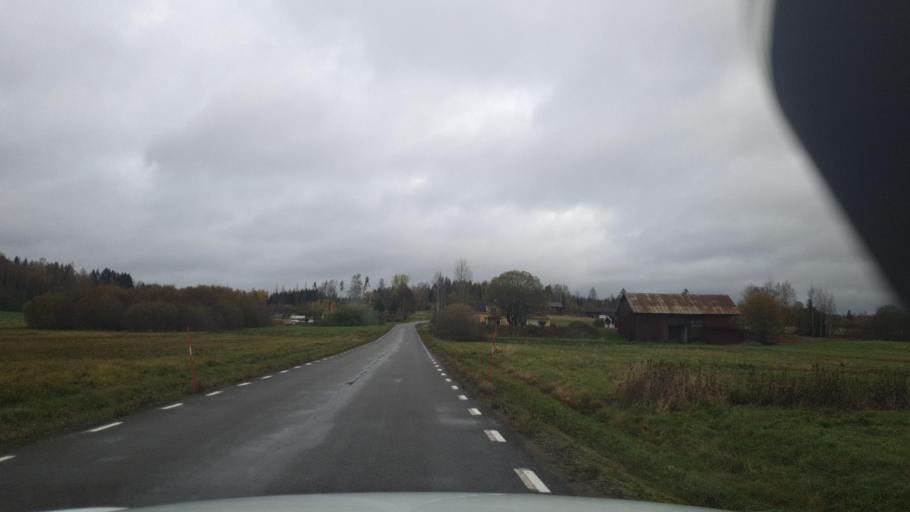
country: SE
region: Vaermland
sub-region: Eda Kommun
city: Amotfors
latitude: 59.7119
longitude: 12.4490
